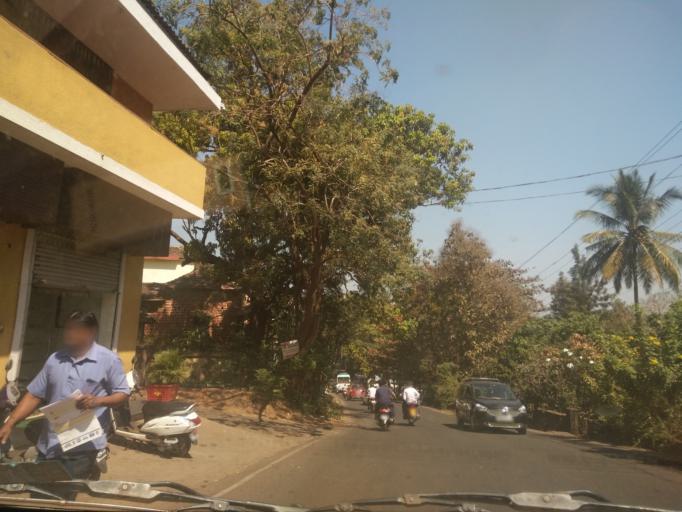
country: IN
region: Goa
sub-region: North Goa
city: Mapuca
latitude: 15.5946
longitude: 73.8148
